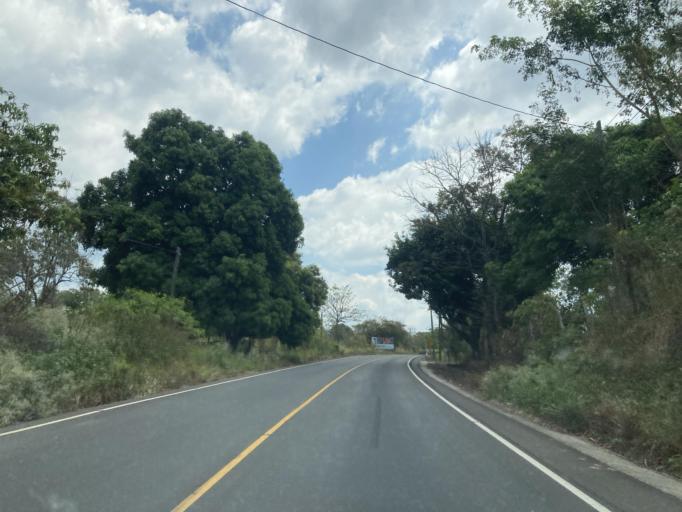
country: GT
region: Santa Rosa
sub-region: Municipio de Taxisco
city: Taxisco
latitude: 14.0894
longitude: -90.5001
